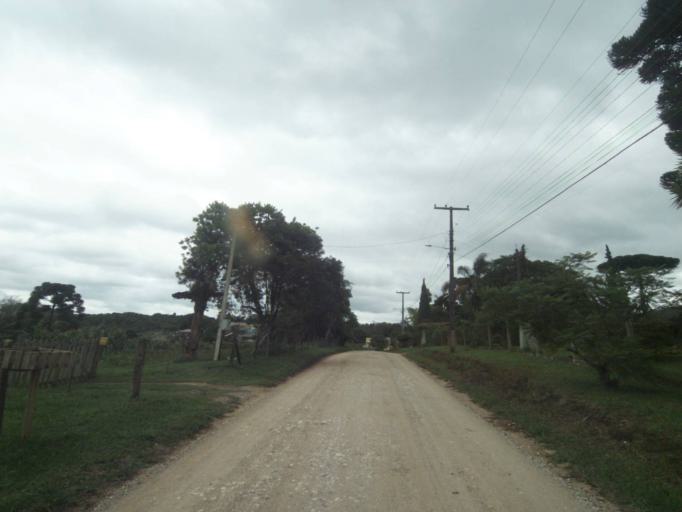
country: BR
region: Parana
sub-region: Quatro Barras
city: Quatro Barras
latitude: -25.3273
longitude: -49.0913
